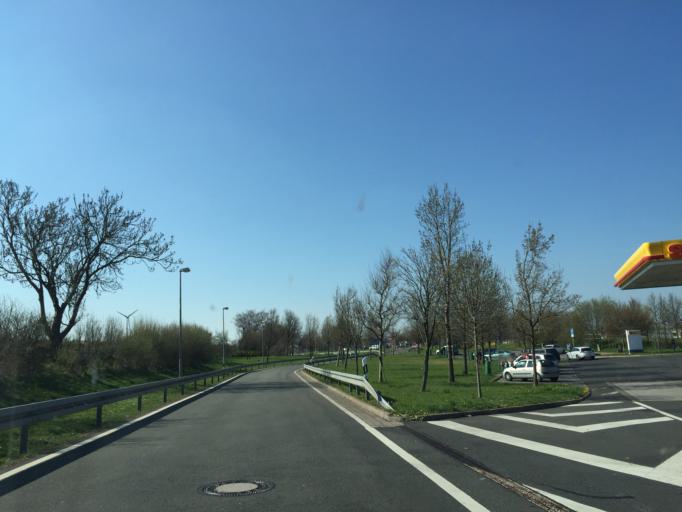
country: DE
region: Thuringia
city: Horselgau
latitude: 50.9109
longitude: 10.5897
